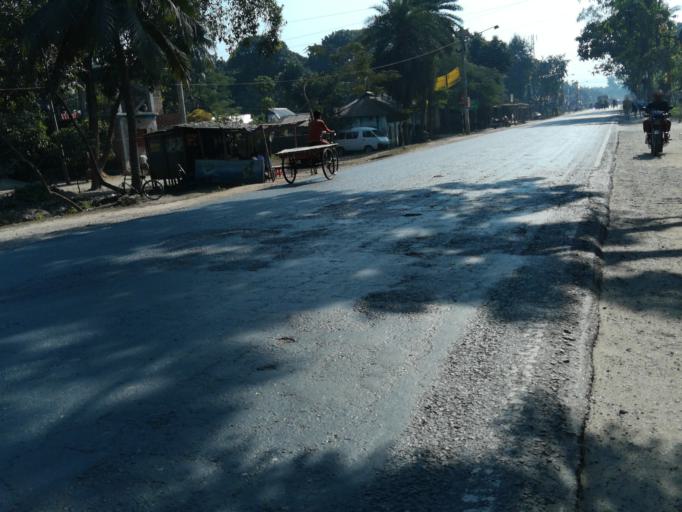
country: BD
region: Rangpur Division
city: Rangpur
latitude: 25.5741
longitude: 89.2745
